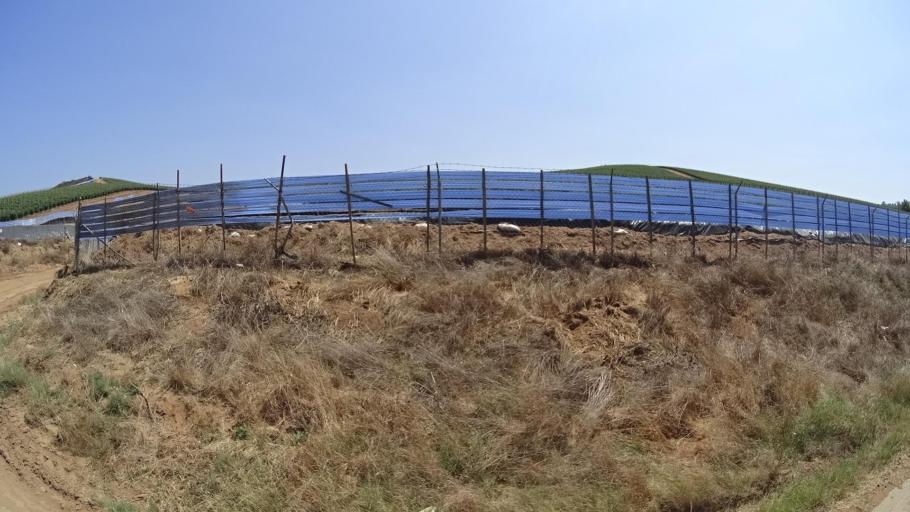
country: US
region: California
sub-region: San Diego County
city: Bonsall
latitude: 33.2704
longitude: -117.2330
